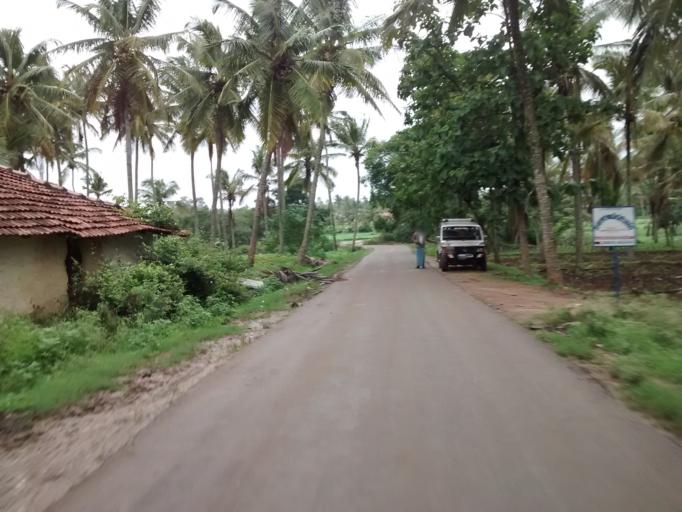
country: IN
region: Karnataka
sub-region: Hassan
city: Hassan
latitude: 12.9300
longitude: 76.1799
